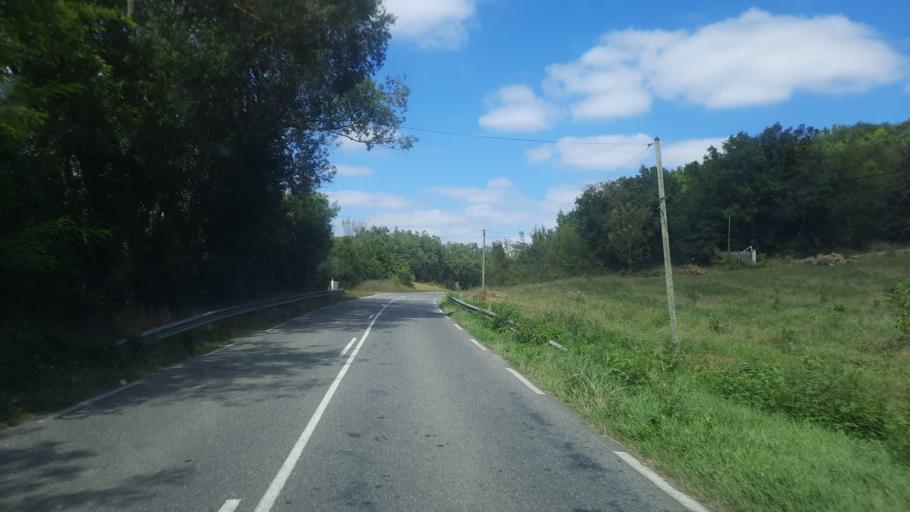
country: FR
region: Midi-Pyrenees
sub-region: Departement du Gers
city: Samatan
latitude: 43.5017
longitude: 0.9713
